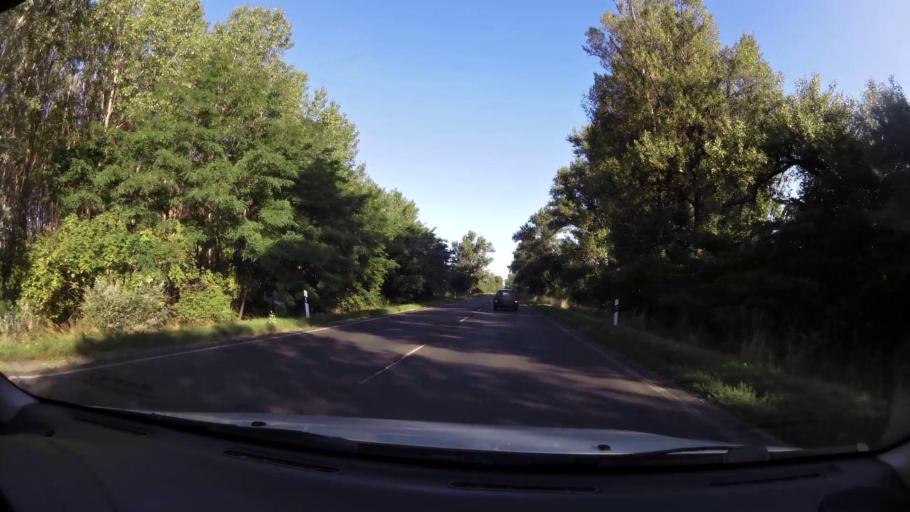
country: HU
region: Pest
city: Pilis
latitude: 47.2936
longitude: 19.5319
